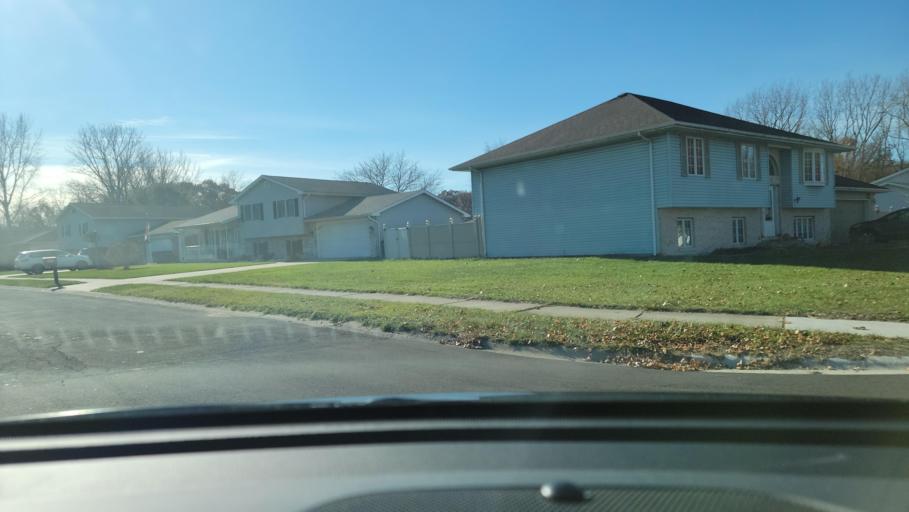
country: US
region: Indiana
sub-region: Porter County
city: Portage
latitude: 41.5891
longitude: -87.1954
